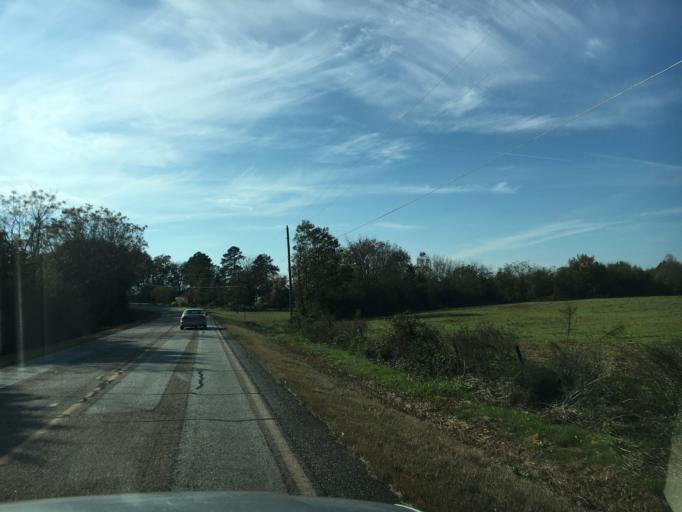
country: US
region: Georgia
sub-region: Hart County
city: Hartwell
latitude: 34.2670
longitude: -82.8903
